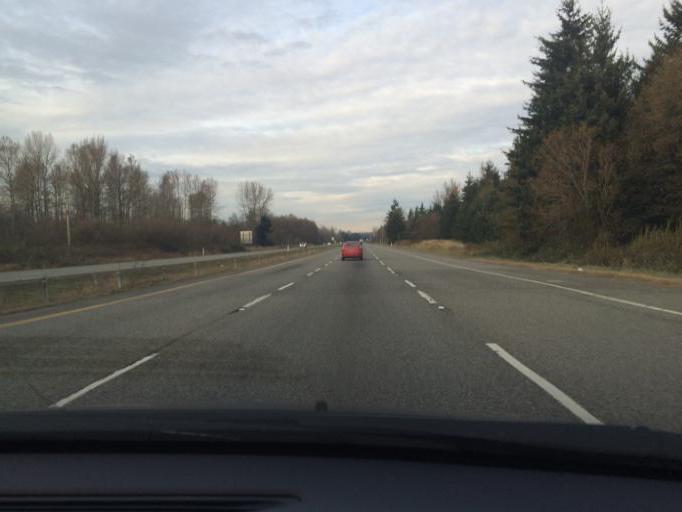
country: US
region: Washington
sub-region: Whatcom County
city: Ferndale
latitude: 48.8631
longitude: -122.5880
